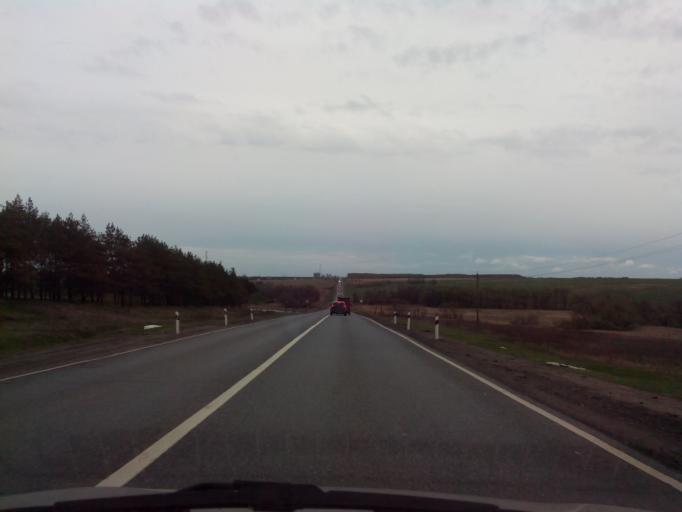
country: RU
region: Moskovskaya
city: Ozherel'ye
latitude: 54.7239
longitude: 38.2730
